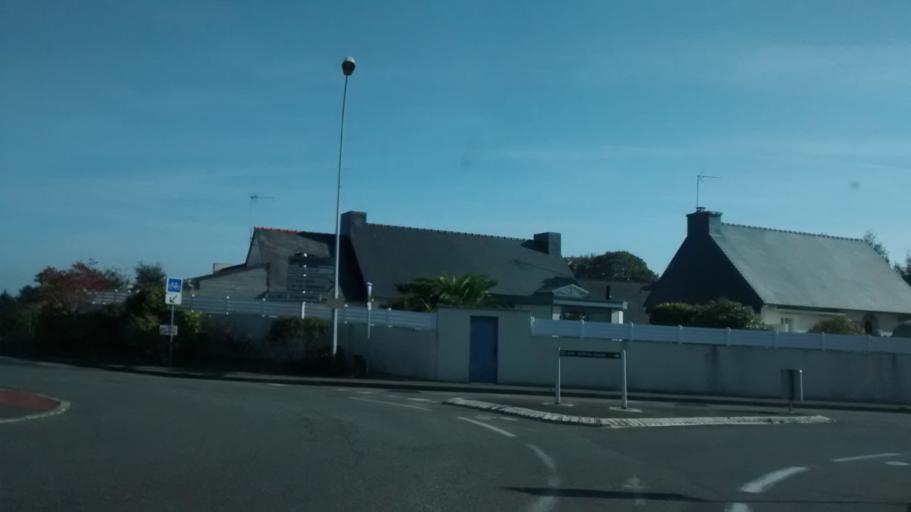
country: FR
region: Brittany
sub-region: Departement des Cotes-d'Armor
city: Lannion
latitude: 48.7469
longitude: -3.4595
